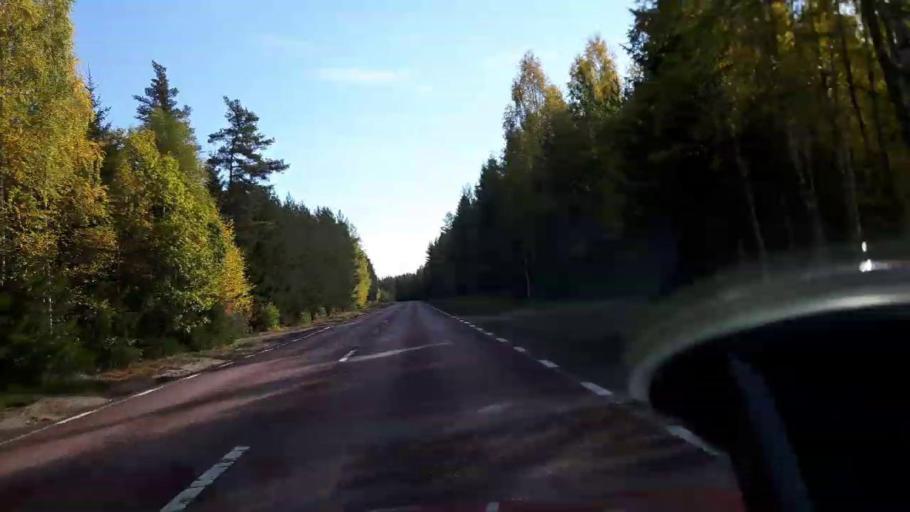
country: SE
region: Gaevleborg
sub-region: Ljusdals Kommun
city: Farila
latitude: 61.9269
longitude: 15.5713
